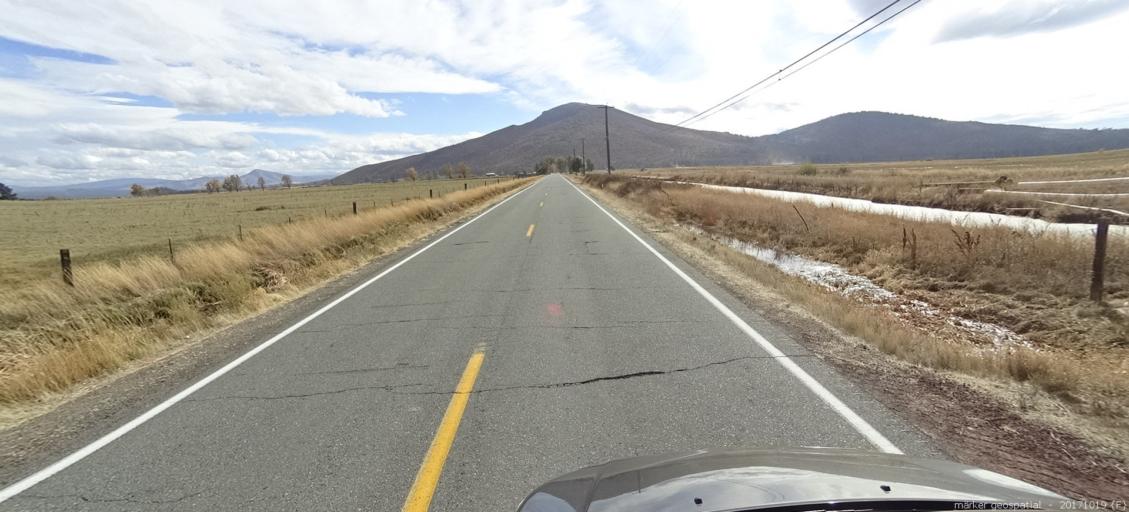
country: US
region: California
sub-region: Shasta County
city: Burney
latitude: 41.0578
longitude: -121.4948
